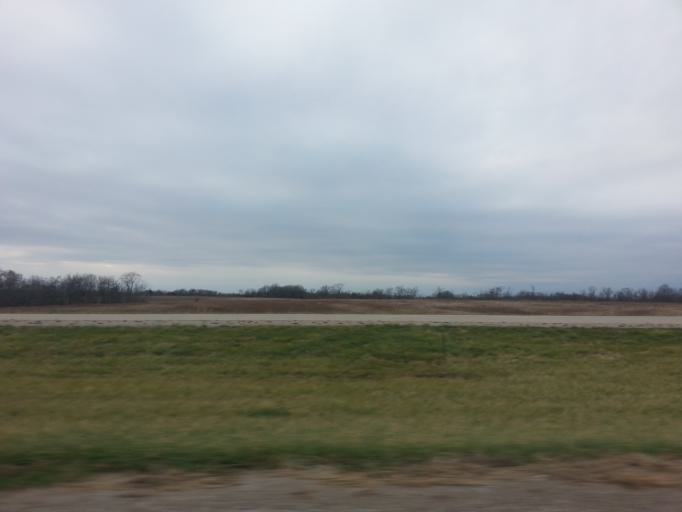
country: US
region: Iowa
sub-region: Henry County
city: Mount Pleasant
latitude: 40.8770
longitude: -91.5650
